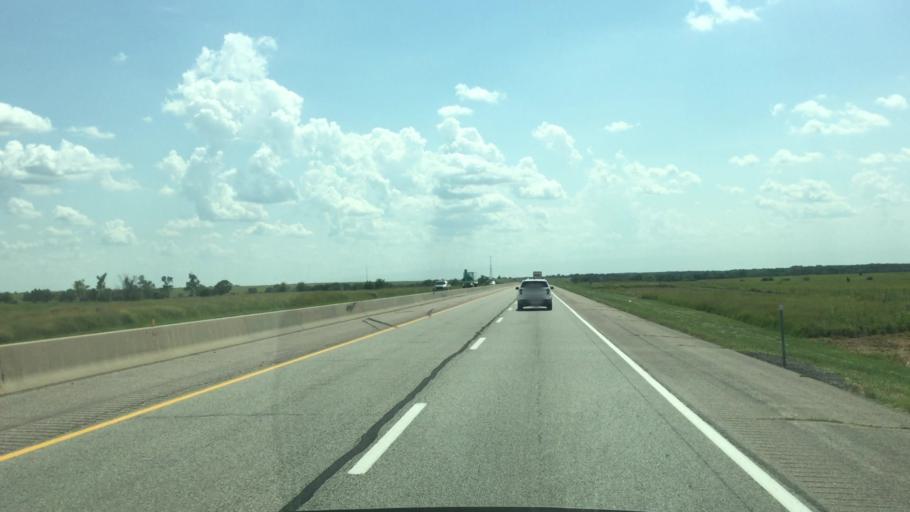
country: US
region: Kansas
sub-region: Butler County
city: El Dorado
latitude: 37.9785
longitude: -96.7138
